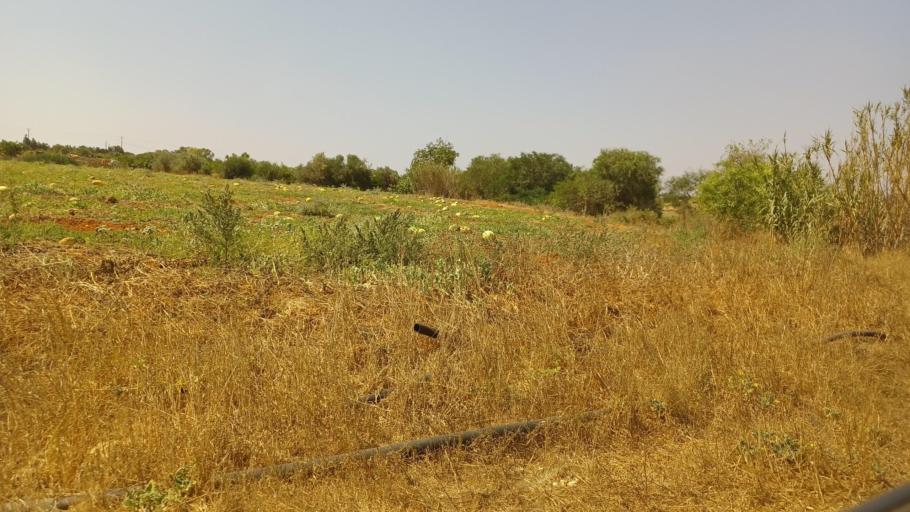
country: CY
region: Ammochostos
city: Frenaros
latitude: 35.0626
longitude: 33.9192
